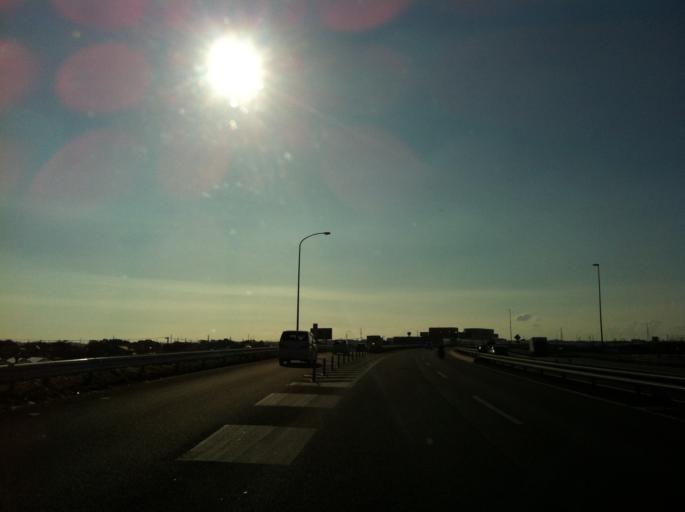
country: JP
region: Aichi
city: Toyohashi
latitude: 34.7301
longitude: 137.3536
